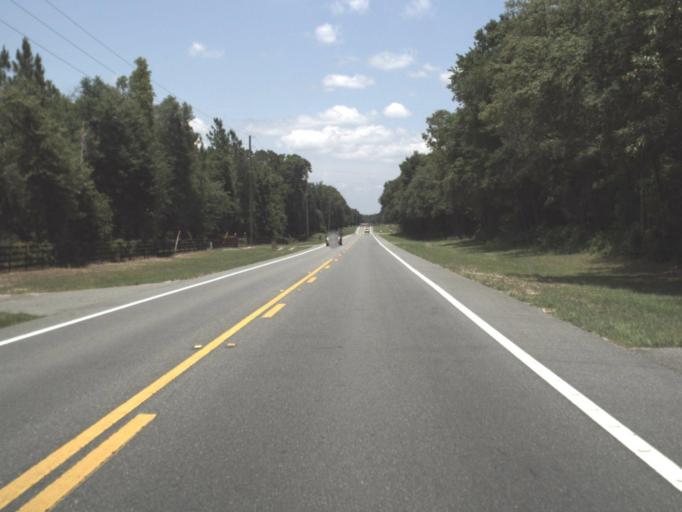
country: US
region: Florida
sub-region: Levy County
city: Williston
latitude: 29.4223
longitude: -82.4245
